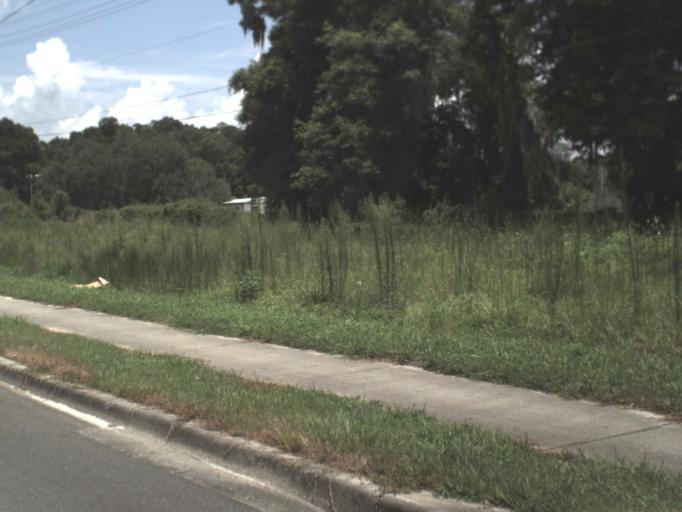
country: US
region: Florida
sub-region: Alachua County
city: Gainesville
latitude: 29.6055
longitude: -82.4085
